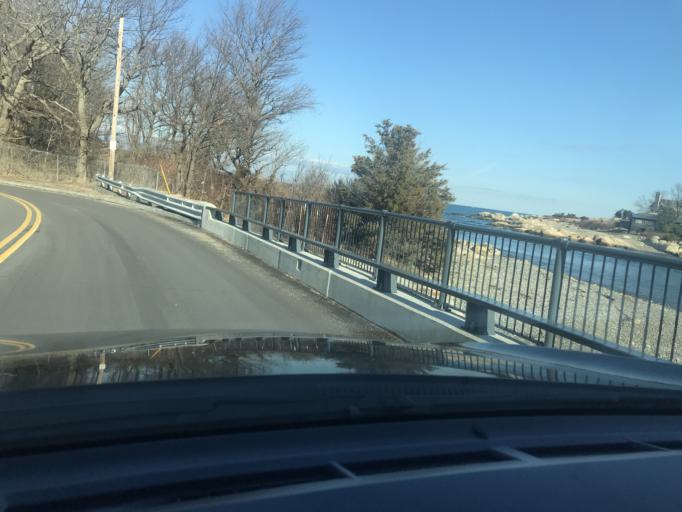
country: US
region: Massachusetts
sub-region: Norfolk County
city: Cohasset
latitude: 42.2525
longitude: -70.7950
